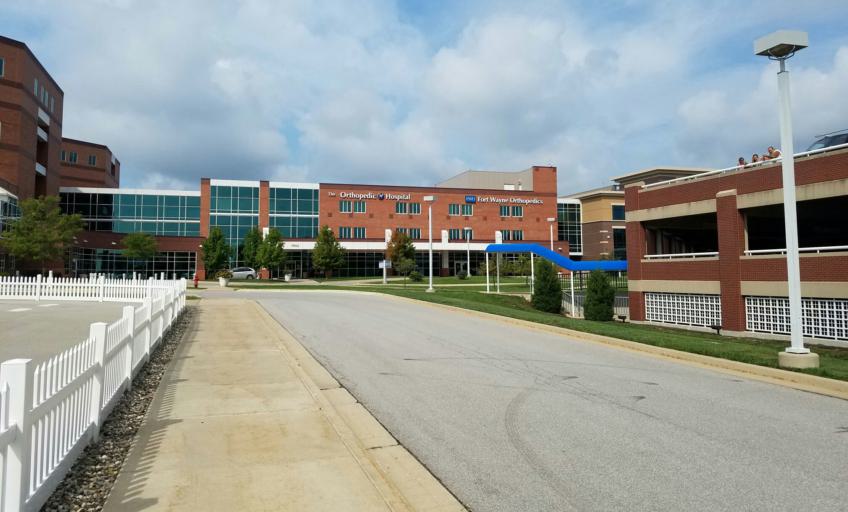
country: US
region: Indiana
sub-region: Huntington County
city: Roanoke
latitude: 41.0395
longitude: -85.2484
